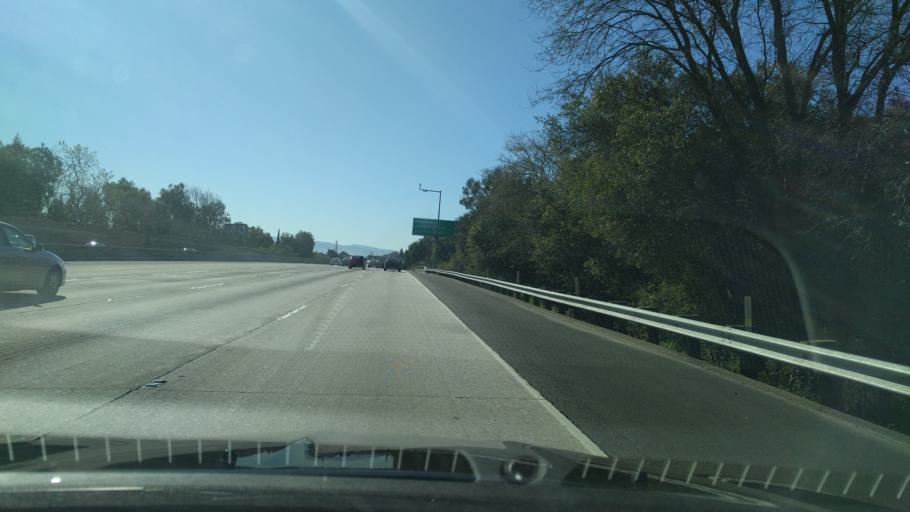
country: US
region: California
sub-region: Contra Costa County
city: San Ramon
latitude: 37.7484
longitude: -121.9581
